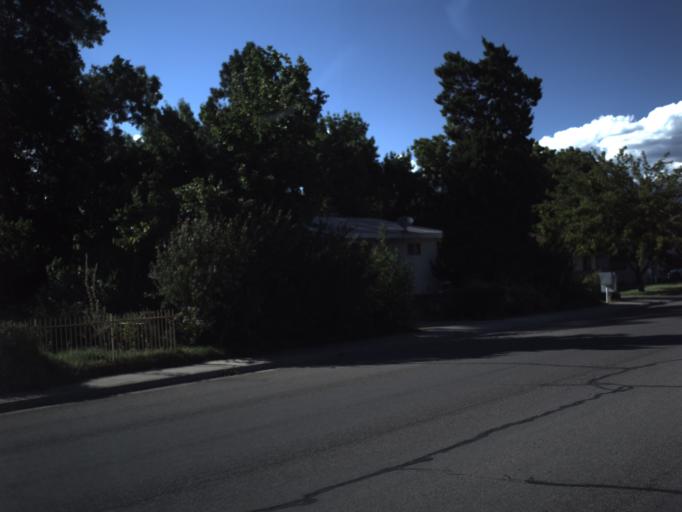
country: US
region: Utah
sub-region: Washington County
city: Hurricane
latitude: 37.1782
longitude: -113.2881
